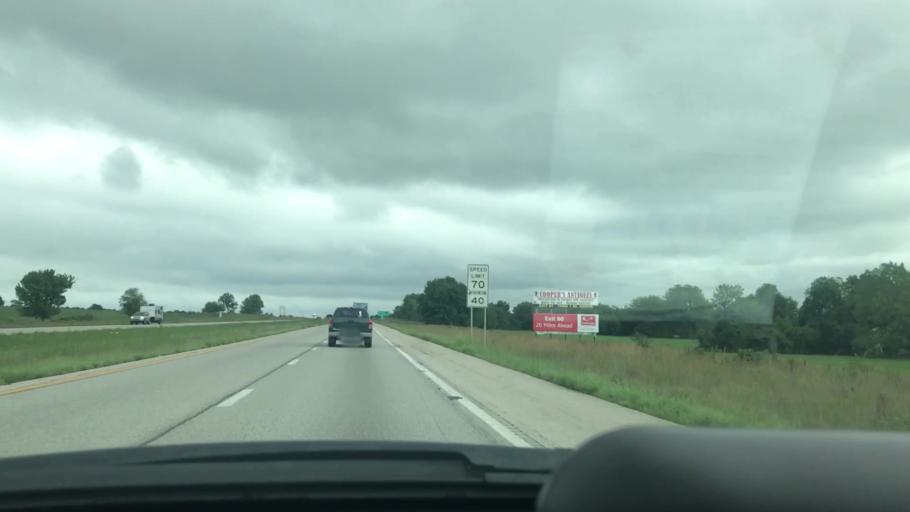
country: US
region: Missouri
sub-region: Greene County
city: Ash Grove
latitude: 37.1872
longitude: -93.6220
